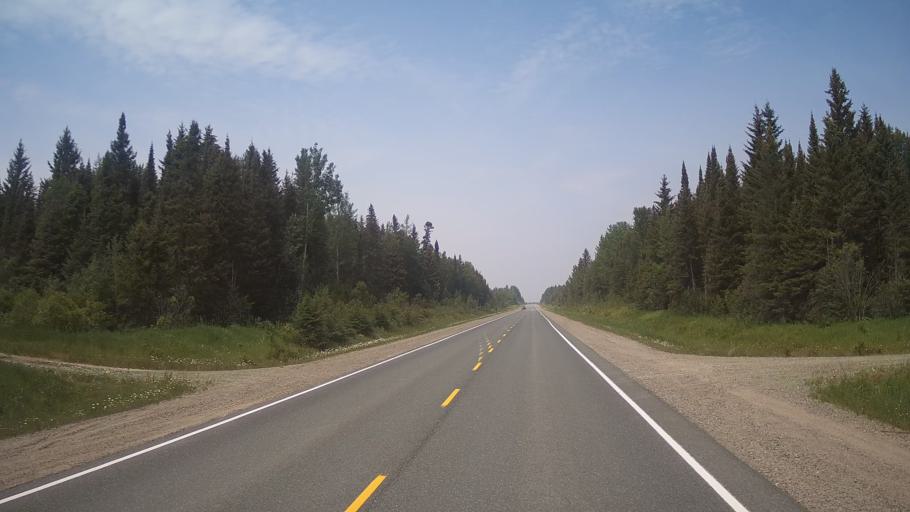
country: CA
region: Ontario
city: Timmins
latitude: 48.7401
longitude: -81.3560
